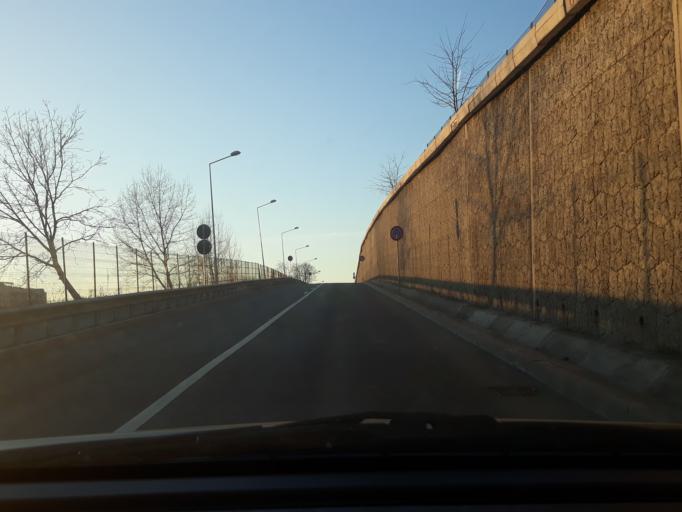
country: RO
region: Bihor
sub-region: Comuna Biharea
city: Oradea
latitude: 47.0536
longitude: 21.9547
